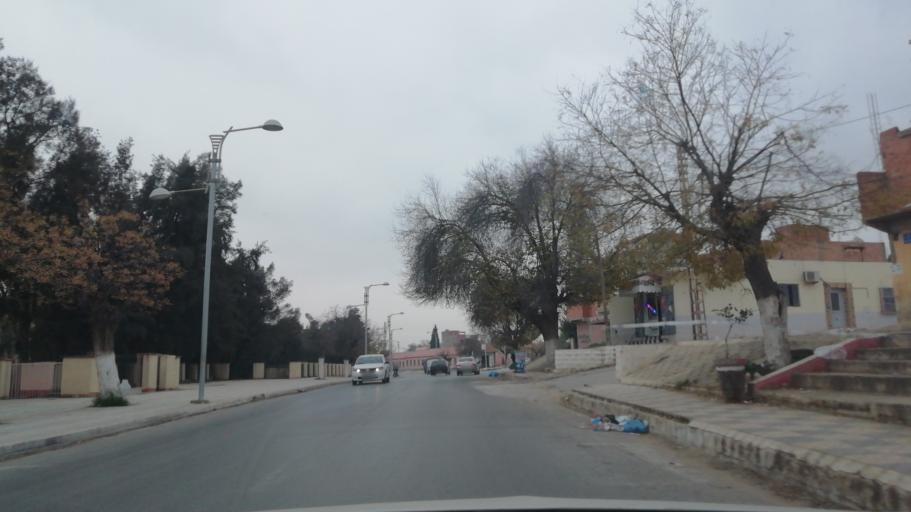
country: DZ
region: Sidi Bel Abbes
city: Sfizef
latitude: 35.2377
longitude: -0.2385
